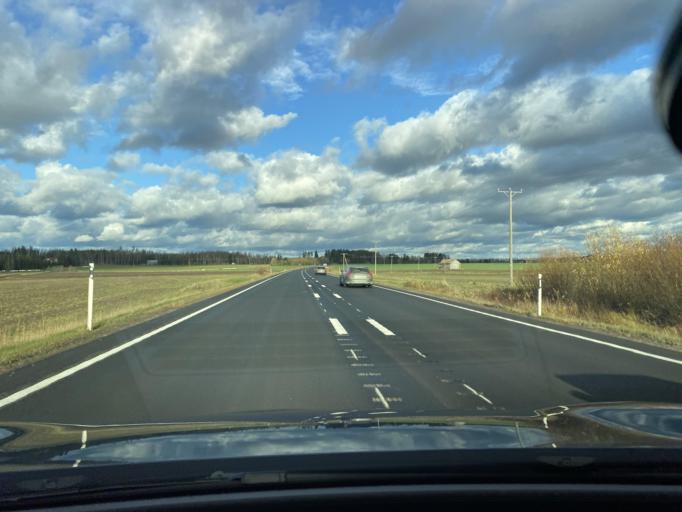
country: FI
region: Haeme
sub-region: Riihimaeki
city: Oitti
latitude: 60.8293
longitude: 25.0796
